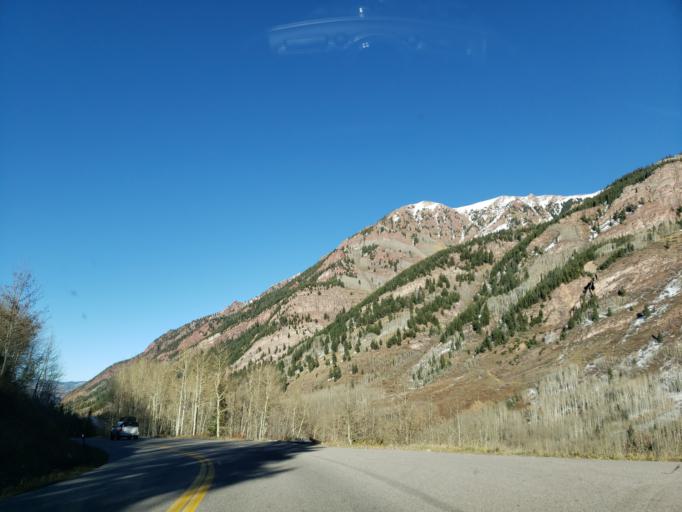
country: US
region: Colorado
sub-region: Pitkin County
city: Snowmass Village
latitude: 39.1107
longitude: -106.9139
